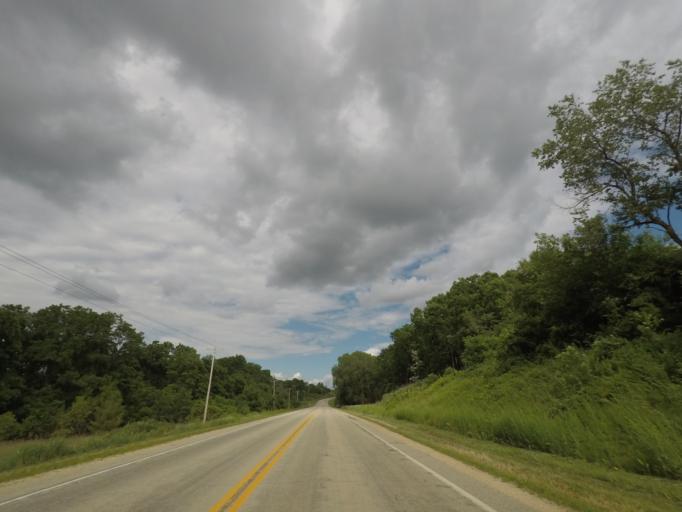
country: US
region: Wisconsin
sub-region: Green County
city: Brooklyn
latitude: 42.8273
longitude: -89.4310
